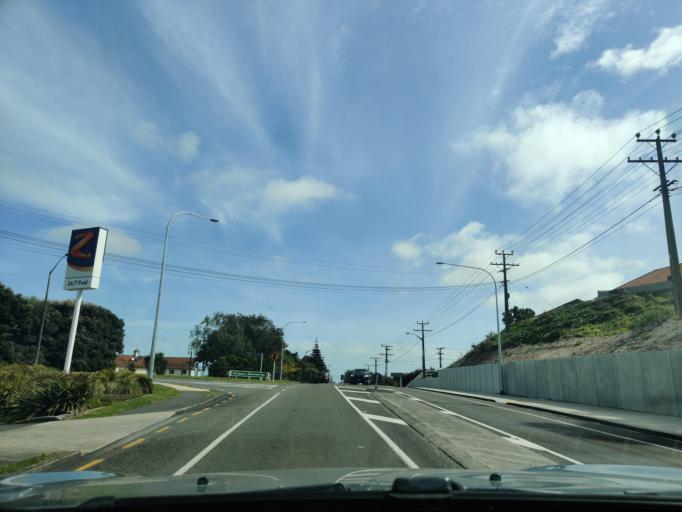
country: NZ
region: Manawatu-Wanganui
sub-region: Wanganui District
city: Wanganui
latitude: -39.9265
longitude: 175.0352
